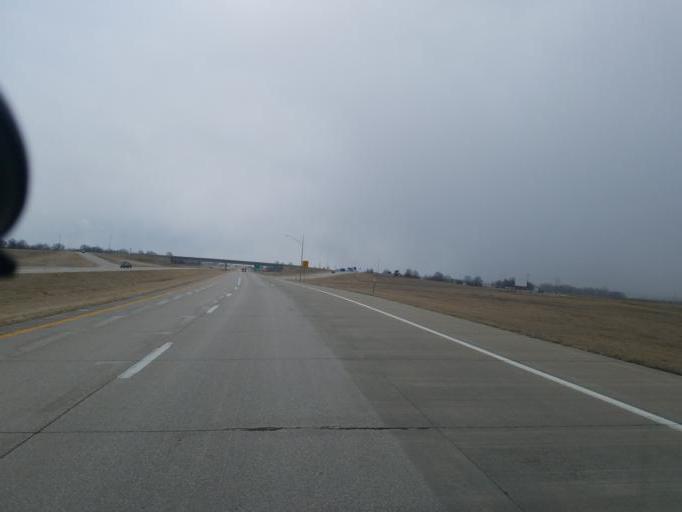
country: US
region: Missouri
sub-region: Randolph County
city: Moberly
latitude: 39.4581
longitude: -92.4342
